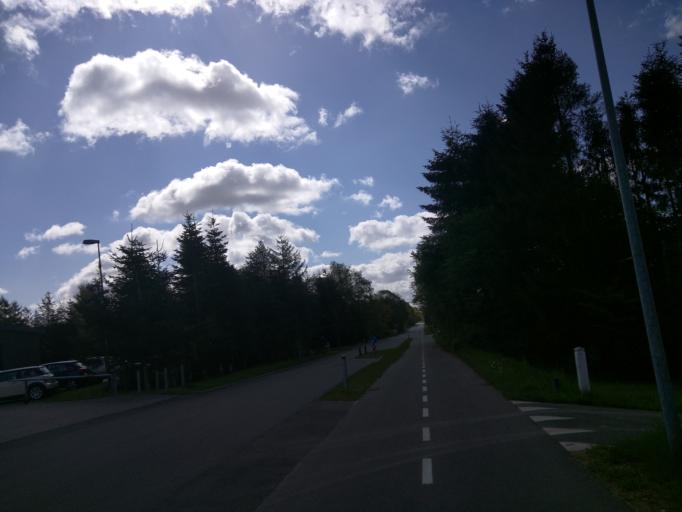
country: DK
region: Central Jutland
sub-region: Viborg Kommune
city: Viborg
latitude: 56.4167
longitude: 9.4099
